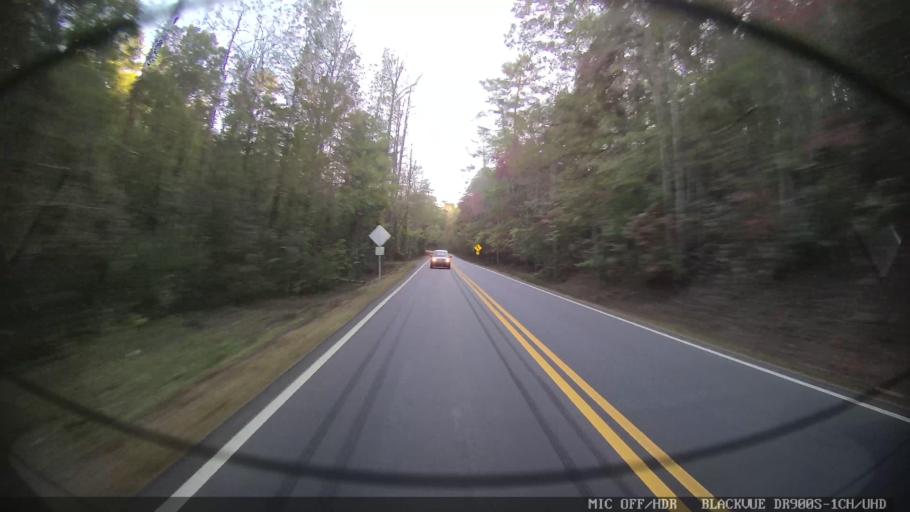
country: US
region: Georgia
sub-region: Lumpkin County
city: Dahlonega
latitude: 34.6337
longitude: -83.9350
